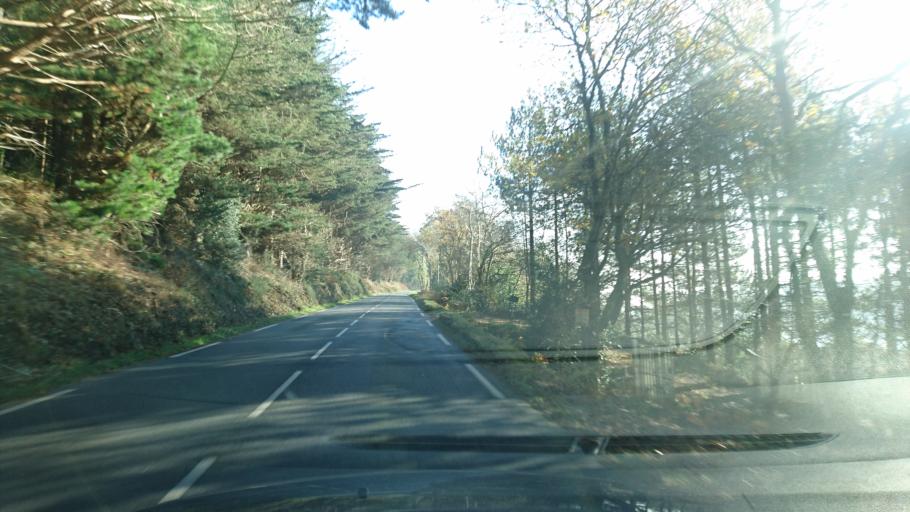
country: FR
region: Brittany
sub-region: Departement du Finistere
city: Logonna-Daoulas
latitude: 48.2766
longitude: -4.2746
